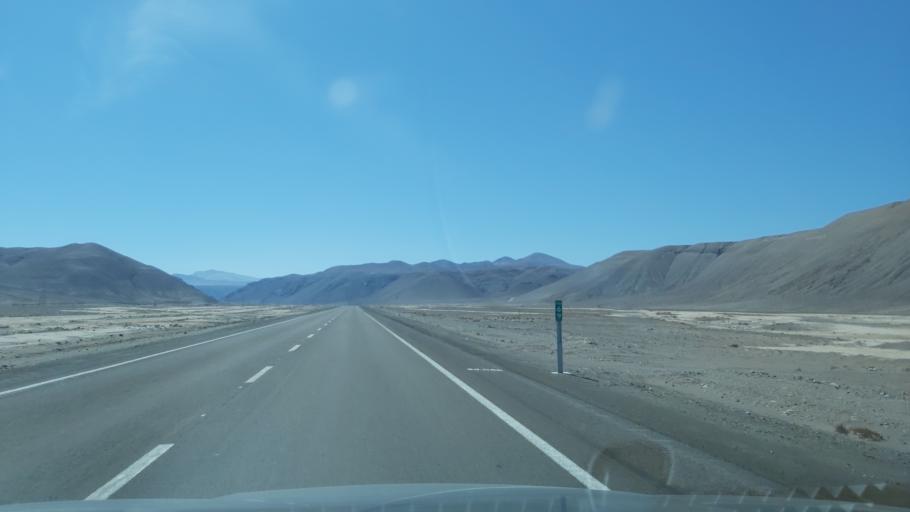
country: CL
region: Atacama
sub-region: Provincia de Chanaral
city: Diego de Almagro
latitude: -26.3509
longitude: -69.8827
